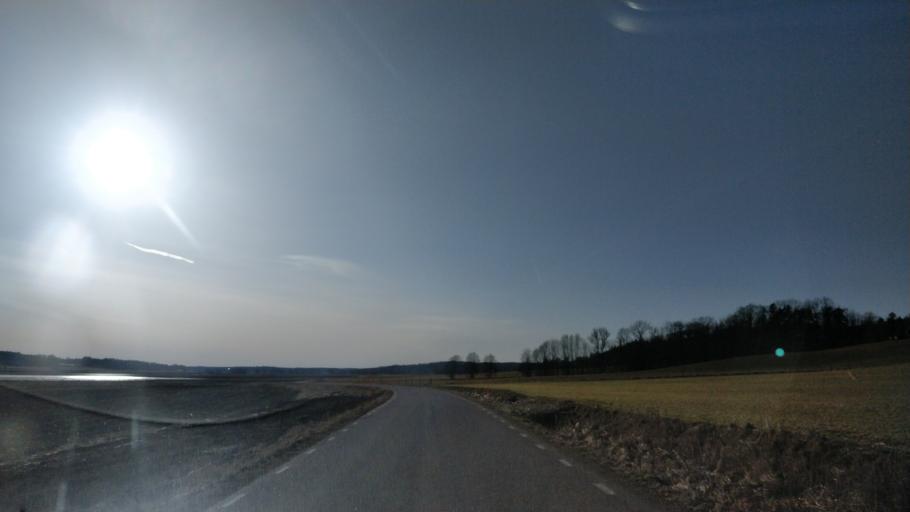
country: SE
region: Uppsala
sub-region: Enkopings Kommun
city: Orsundsbro
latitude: 59.7470
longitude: 17.2008
